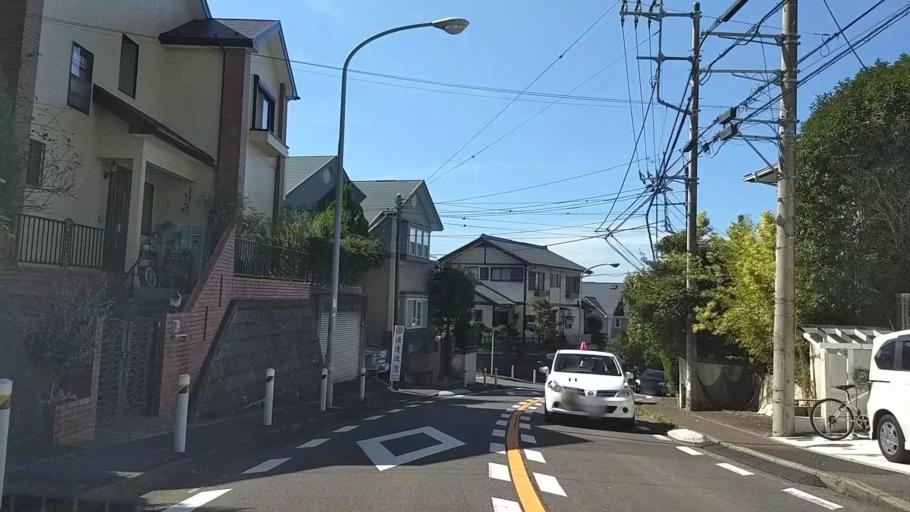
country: JP
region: Tokyo
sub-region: Machida-shi
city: Machida
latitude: 35.5587
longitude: 139.5395
